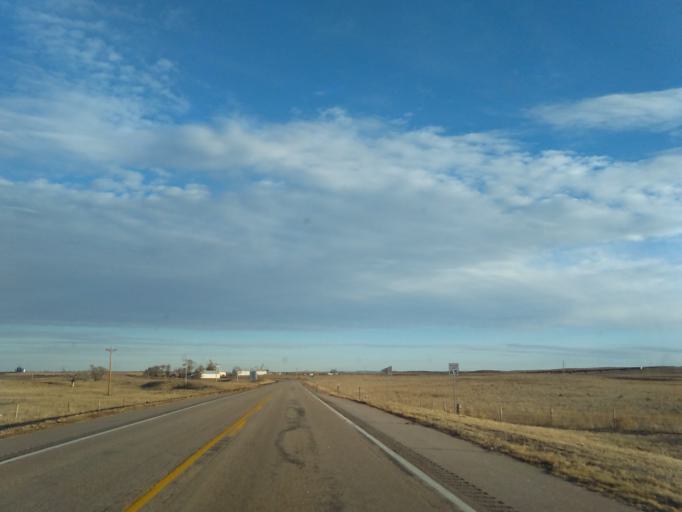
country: US
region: Nebraska
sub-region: Morrill County
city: Bridgeport
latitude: 41.6010
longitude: -102.9816
